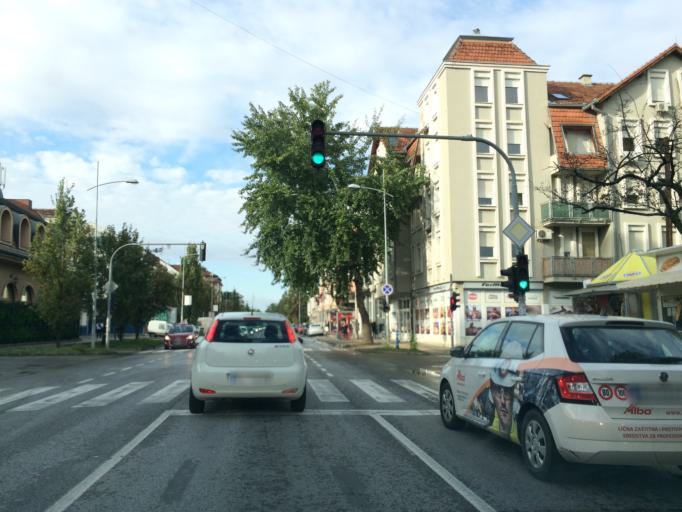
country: RS
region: Autonomna Pokrajina Vojvodina
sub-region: Juznobacki Okrug
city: Novi Sad
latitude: 45.2436
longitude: 19.8252
